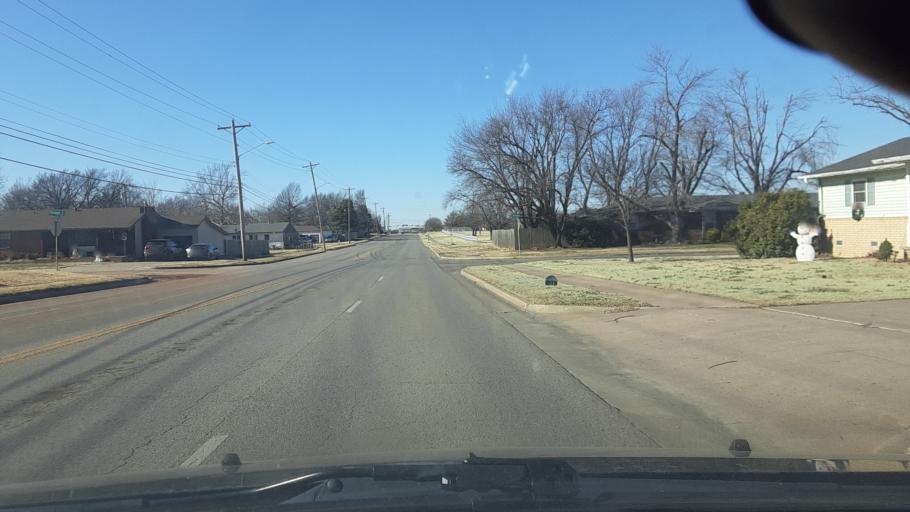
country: US
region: Oklahoma
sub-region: Kay County
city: Ponca City
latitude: 36.7243
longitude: -97.0883
